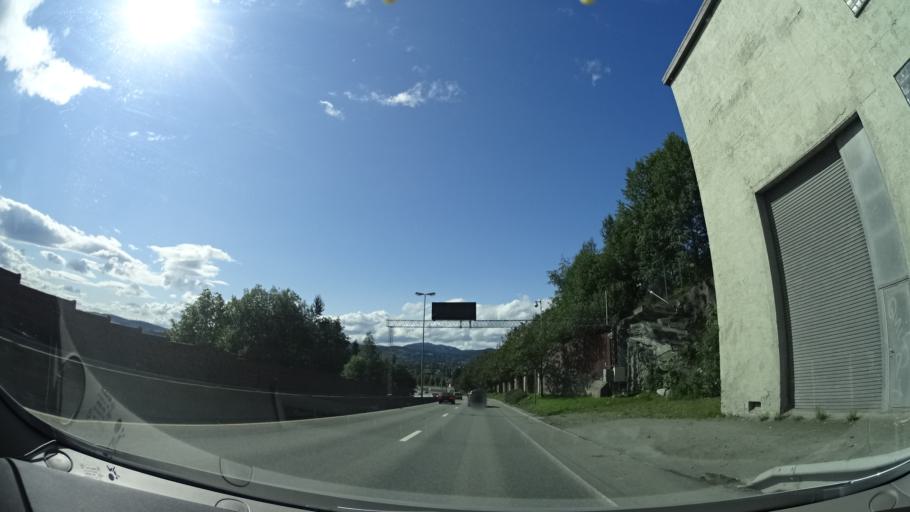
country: NO
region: Sor-Trondelag
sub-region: Trondheim
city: Trondheim
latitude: 63.4077
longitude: 10.4316
